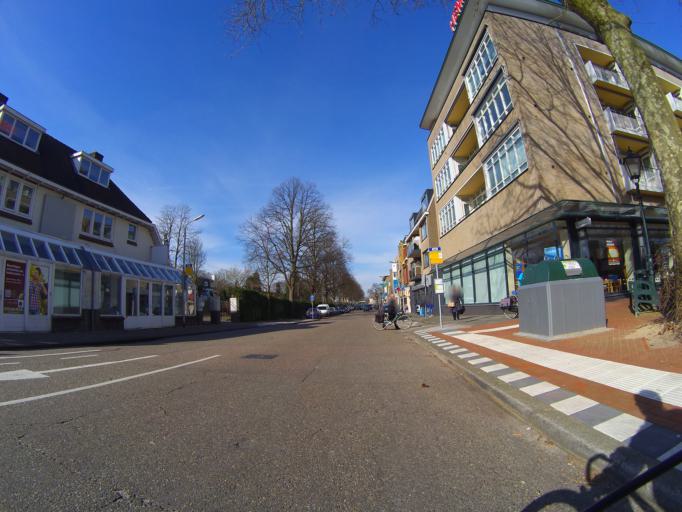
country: NL
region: North Holland
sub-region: Gemeente Bussum
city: Bussum
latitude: 52.2757
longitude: 5.1595
